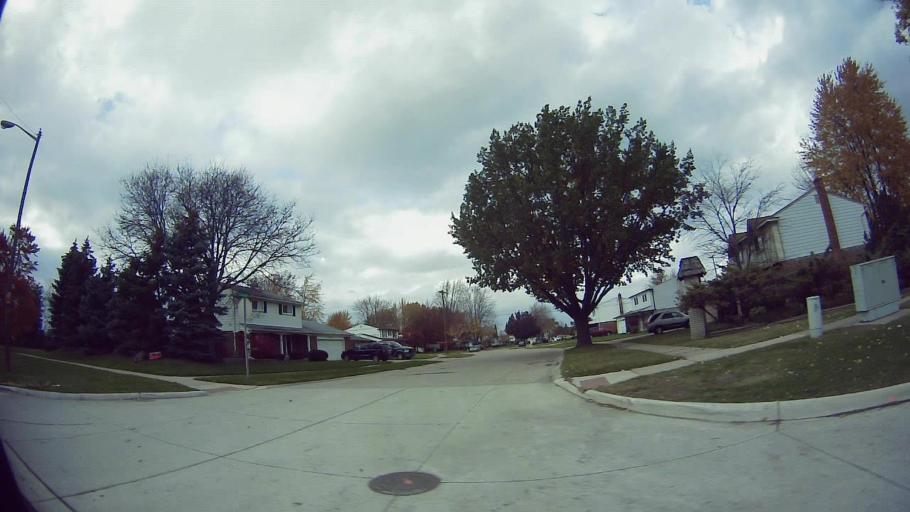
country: US
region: Michigan
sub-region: Macomb County
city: Sterling Heights
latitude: 42.5501
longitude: -83.0667
